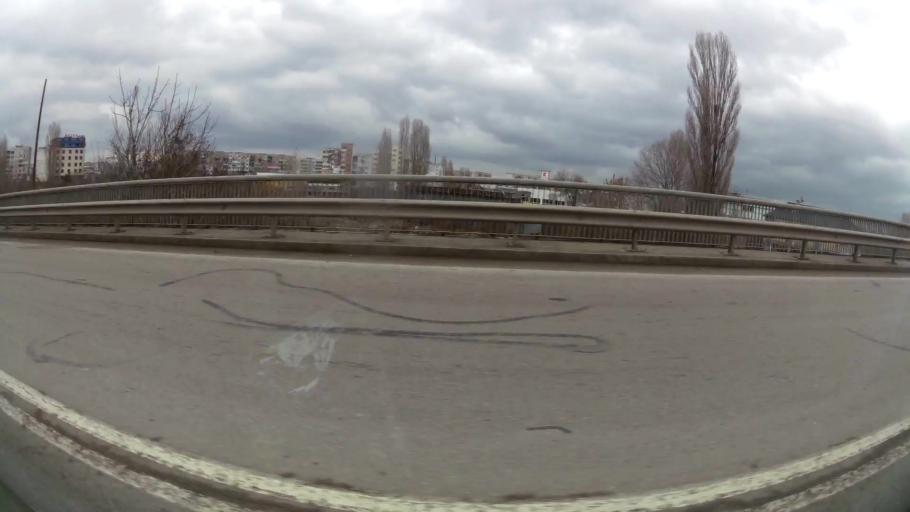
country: BG
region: Sofia-Capital
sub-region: Stolichna Obshtina
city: Sofia
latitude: 42.7303
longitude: 23.2829
